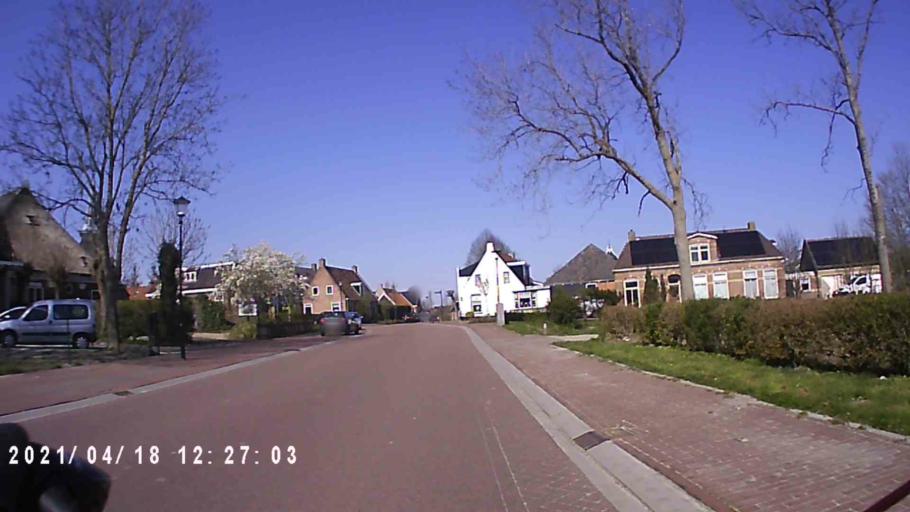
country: NL
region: Friesland
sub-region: Gemeente Dongeradeel
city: Anjum
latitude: 53.3308
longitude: 6.1027
